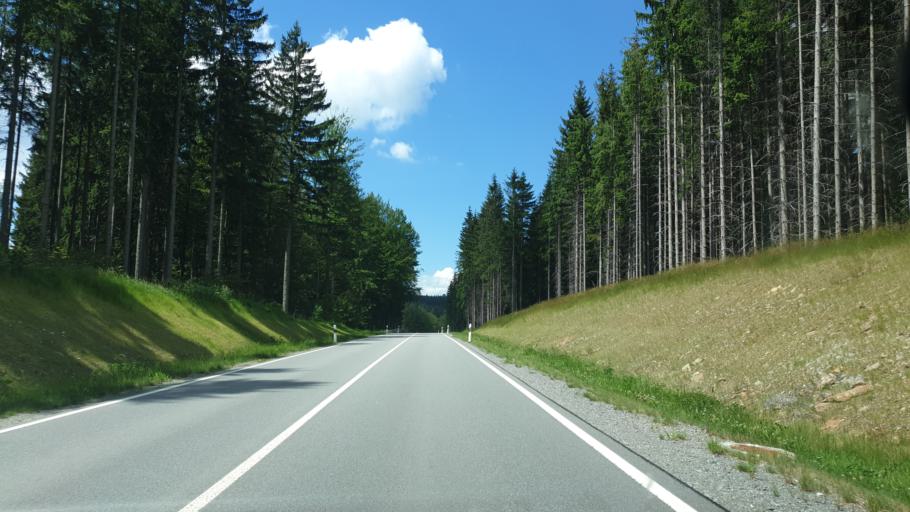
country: DE
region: Saxony
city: Schwarzenberg
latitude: 50.5170
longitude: 12.7500
